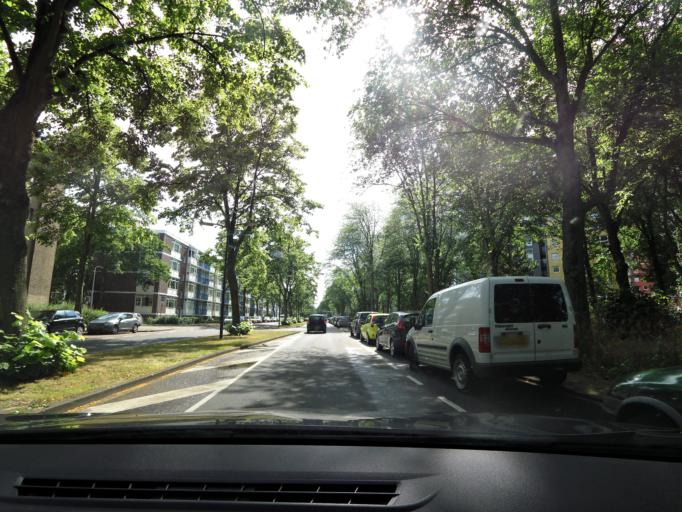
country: NL
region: South Holland
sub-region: Gemeente Westland
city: Kwintsheul
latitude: 52.0447
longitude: 4.2767
